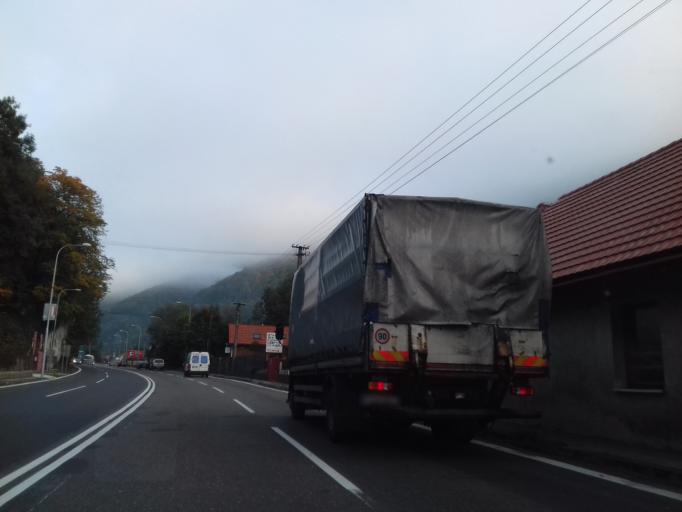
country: SK
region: Banskobystricky
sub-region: Okres Banska Bystrica
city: Banska Bystrica
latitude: 48.7701
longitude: 19.1345
